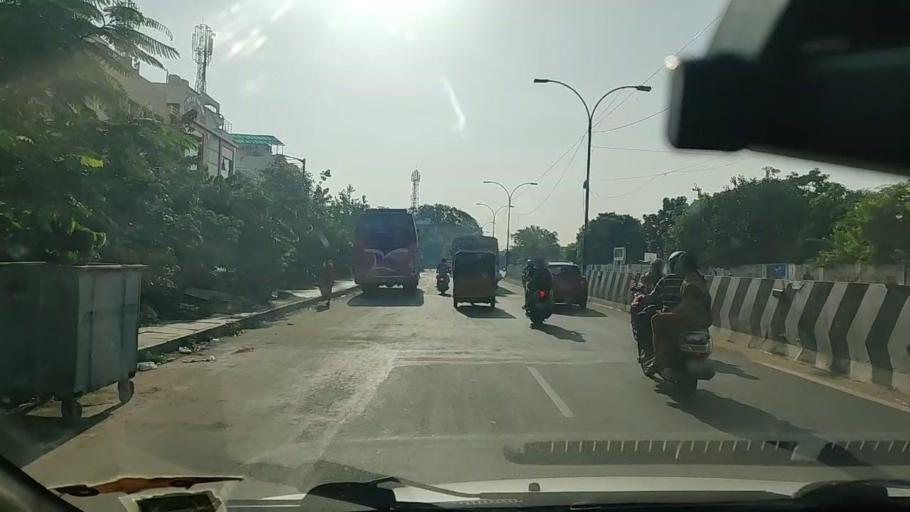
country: IN
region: Tamil Nadu
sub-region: Chennai
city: George Town
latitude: 13.1182
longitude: 80.2600
